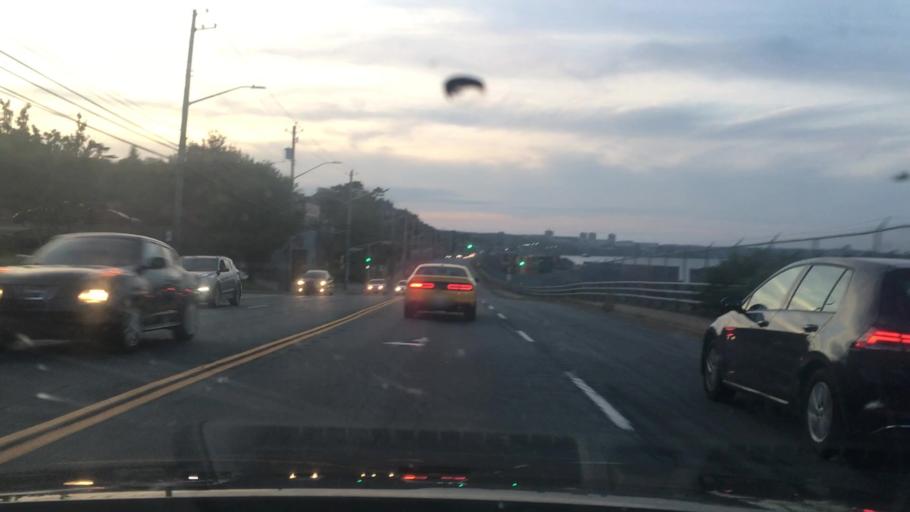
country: CA
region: Nova Scotia
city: Dartmouth
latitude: 44.6656
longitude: -63.6358
